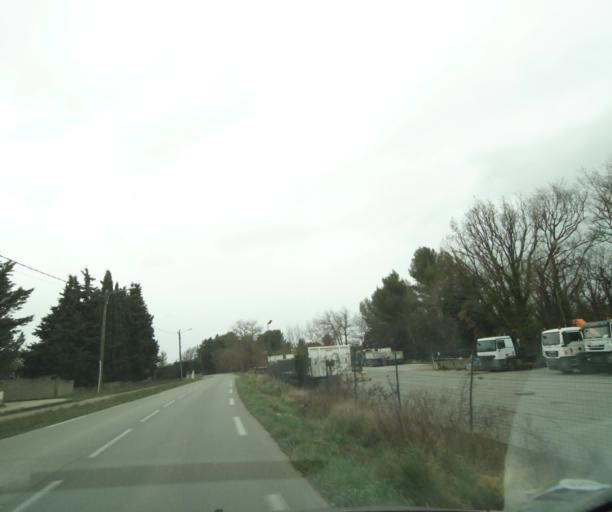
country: FR
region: Provence-Alpes-Cote d'Azur
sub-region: Departement des Bouches-du-Rhone
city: Eguilles
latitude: 43.5757
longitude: 5.4142
